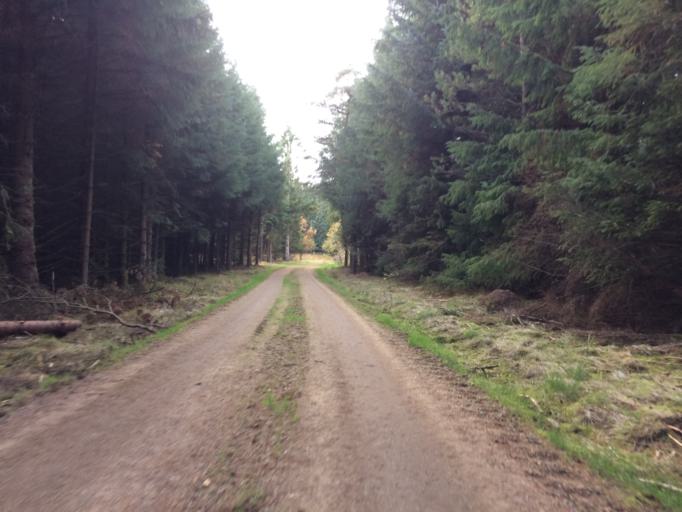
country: DK
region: Central Jutland
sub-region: Holstebro Kommune
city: Ulfborg
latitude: 56.2132
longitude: 8.4651
